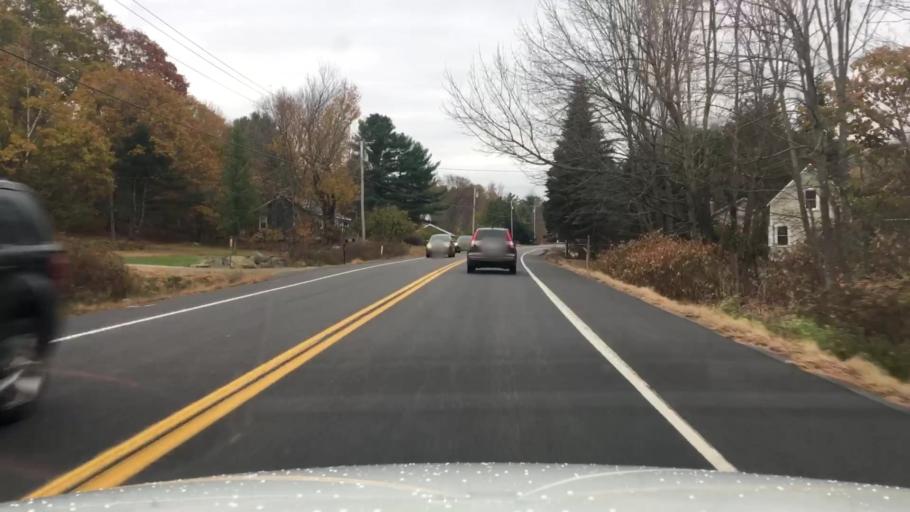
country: US
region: Maine
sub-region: Kennebec County
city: Pittston
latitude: 44.1811
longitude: -69.7462
